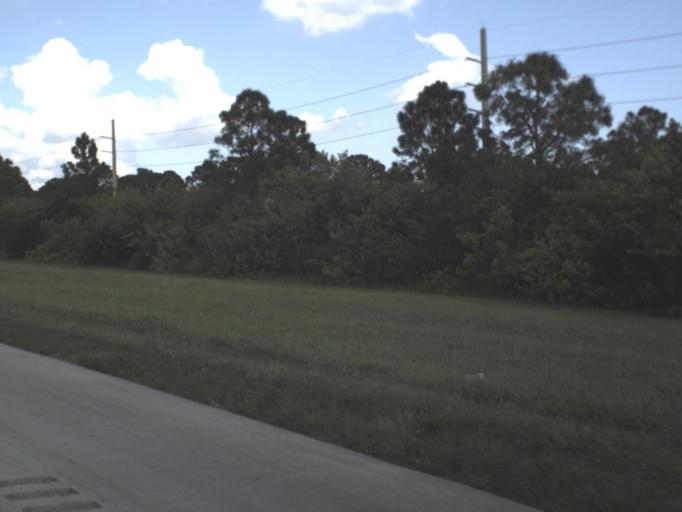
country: US
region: Florida
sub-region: Martin County
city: Palm City
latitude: 27.1384
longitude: -80.2889
